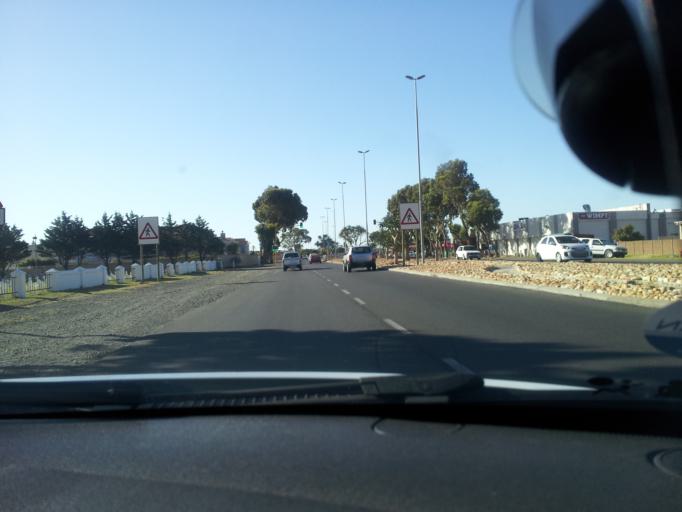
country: ZA
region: Western Cape
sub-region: Overberg District Municipality
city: Grabouw
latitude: -34.1481
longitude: 18.8576
